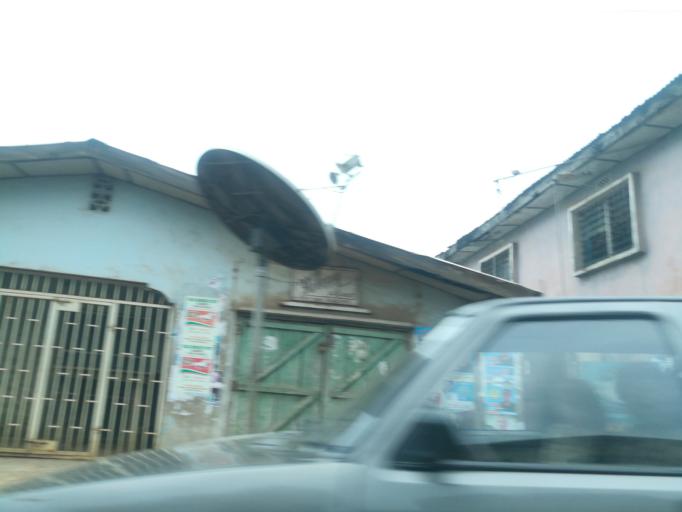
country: NG
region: Oyo
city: Ibadan
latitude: 7.4449
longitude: 3.9123
